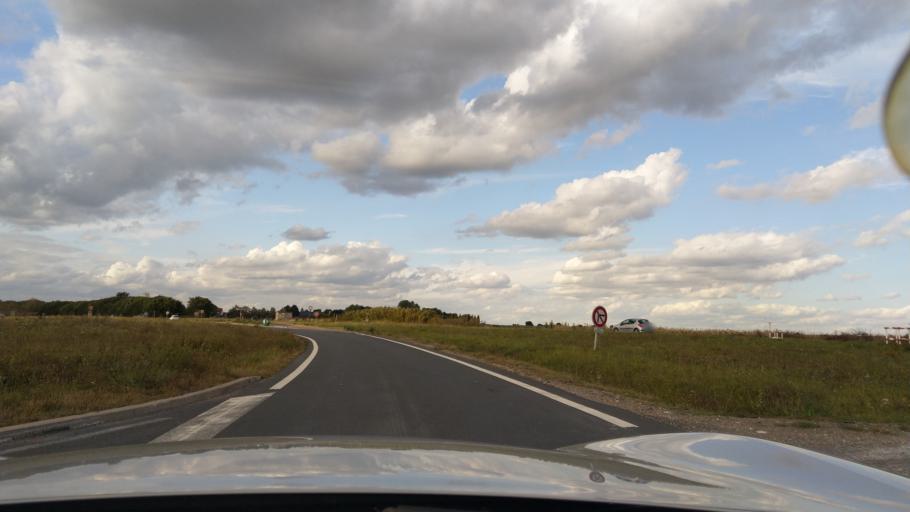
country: FR
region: Ile-de-France
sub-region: Departement de Seine-et-Marne
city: Moussy-le-Neuf
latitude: 49.0248
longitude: 2.5842
